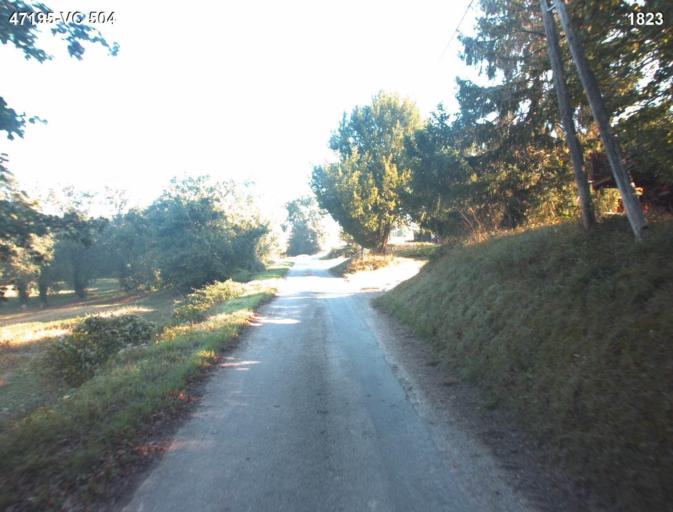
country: FR
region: Aquitaine
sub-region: Departement du Lot-et-Garonne
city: Nerac
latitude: 44.1627
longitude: 0.3351
